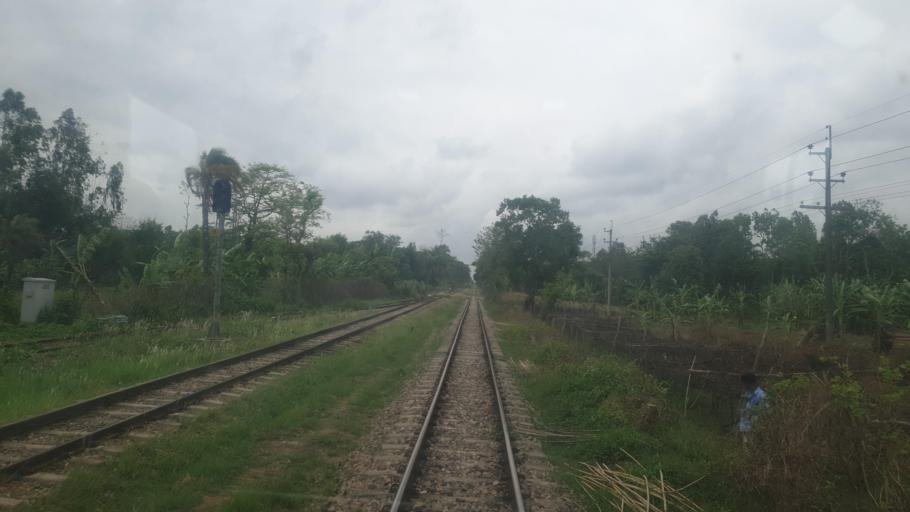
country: BD
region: Chittagong
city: Fatikchari
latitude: 22.6797
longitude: 91.6334
